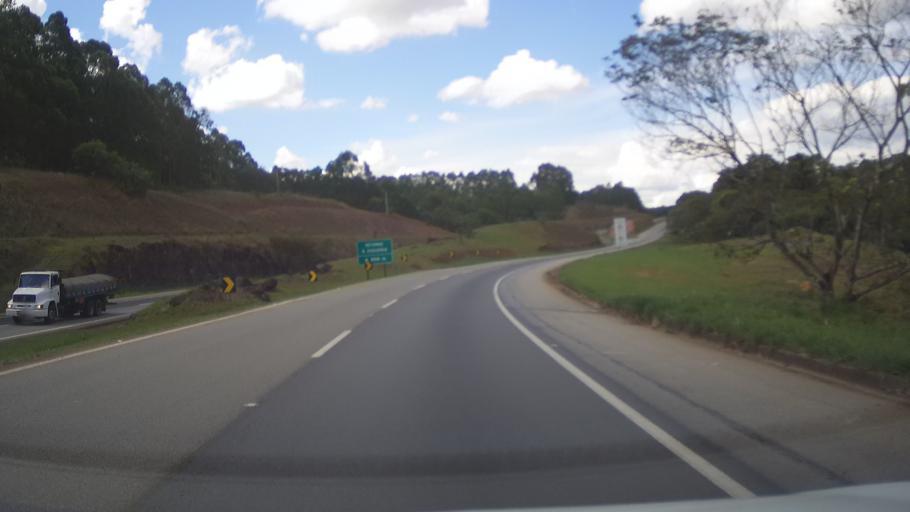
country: BR
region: Minas Gerais
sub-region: Santo Antonio Do Amparo
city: Santo Antonio do Amparo
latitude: -20.8556
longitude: -44.8370
